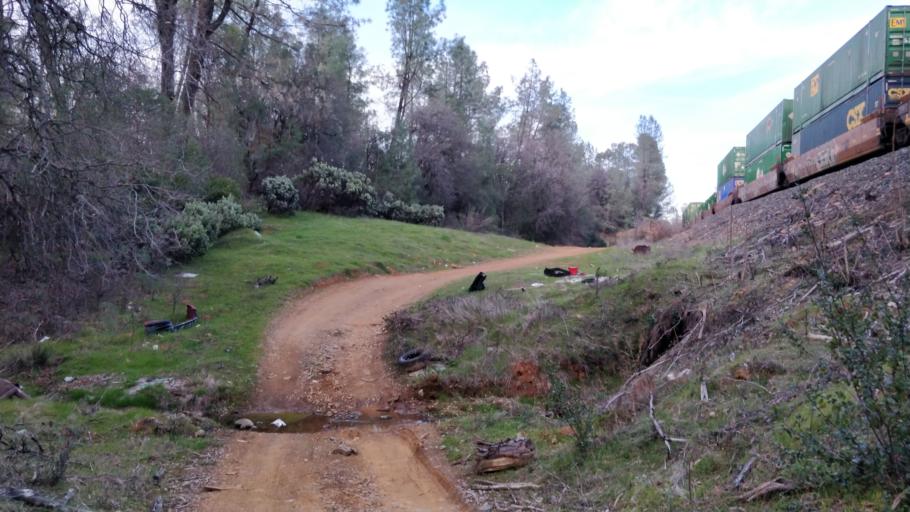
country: US
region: California
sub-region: Shasta County
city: Central Valley (historical)
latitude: 40.6413
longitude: -122.3965
